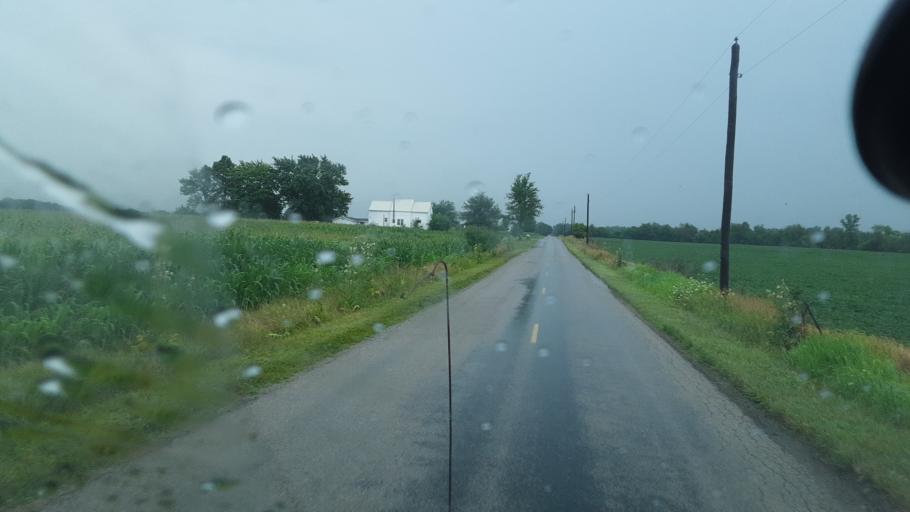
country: US
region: Ohio
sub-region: Williams County
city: Edgerton
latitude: 41.4972
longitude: -84.8149
